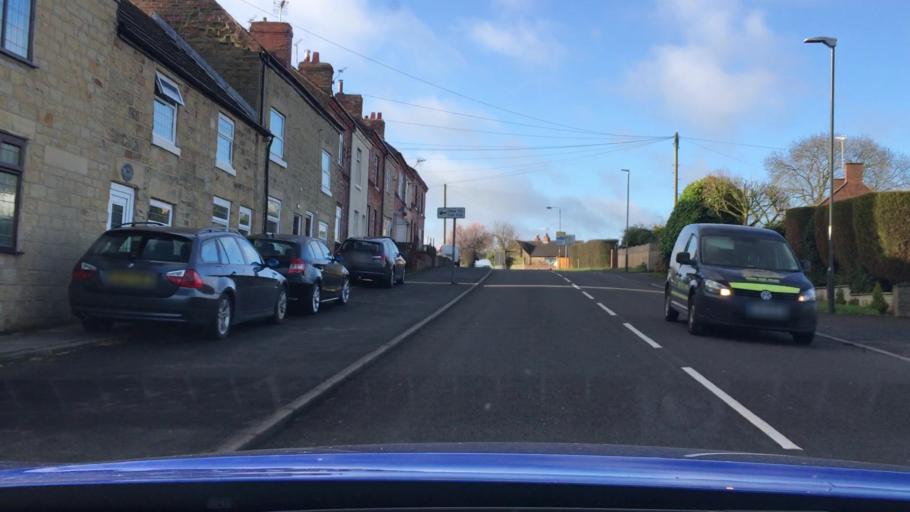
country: GB
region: England
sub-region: Derbyshire
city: Tibshelf
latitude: 53.1486
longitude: -1.3358
